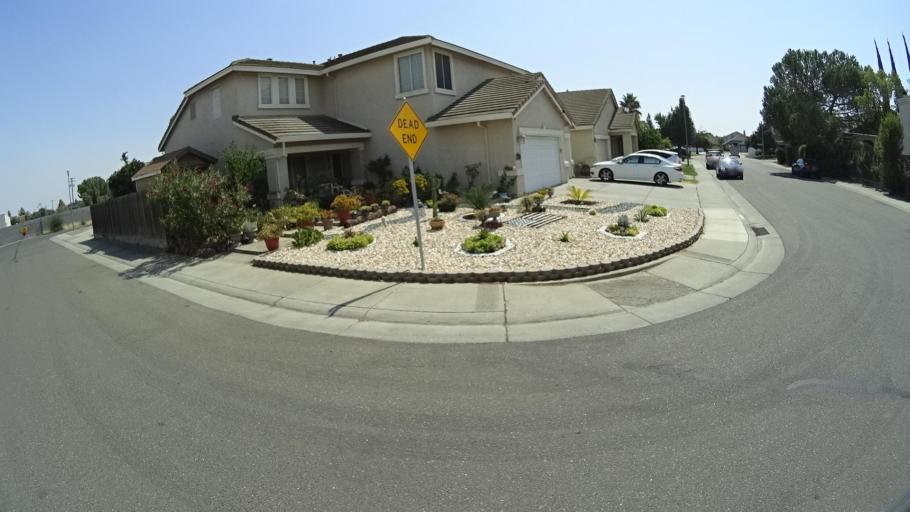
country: US
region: California
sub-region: Sacramento County
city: Vineyard
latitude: 38.4504
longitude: -121.3757
